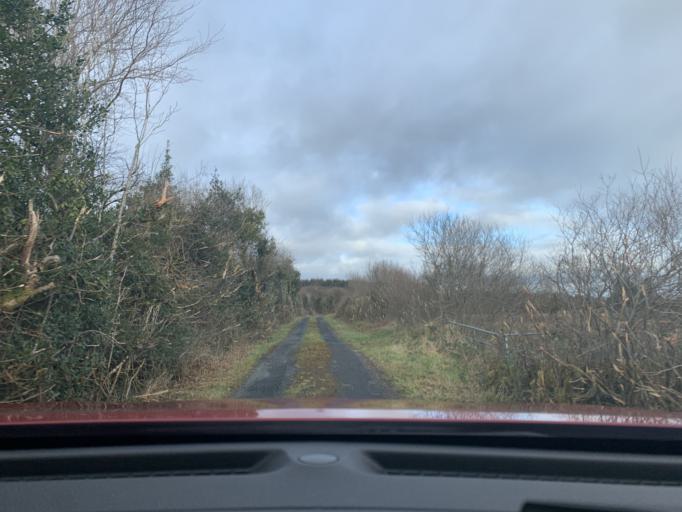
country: IE
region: Connaught
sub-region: Roscommon
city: Ballaghaderreen
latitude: 53.9293
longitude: -8.5588
